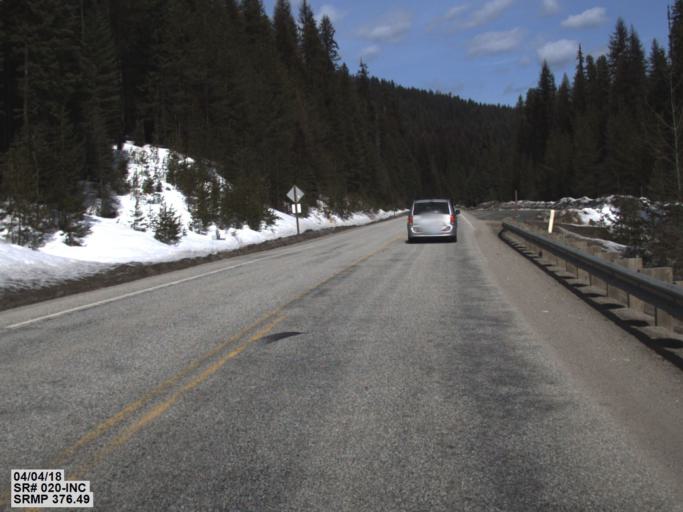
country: US
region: Washington
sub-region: Stevens County
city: Chewelah
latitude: 48.5758
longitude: -117.5560
